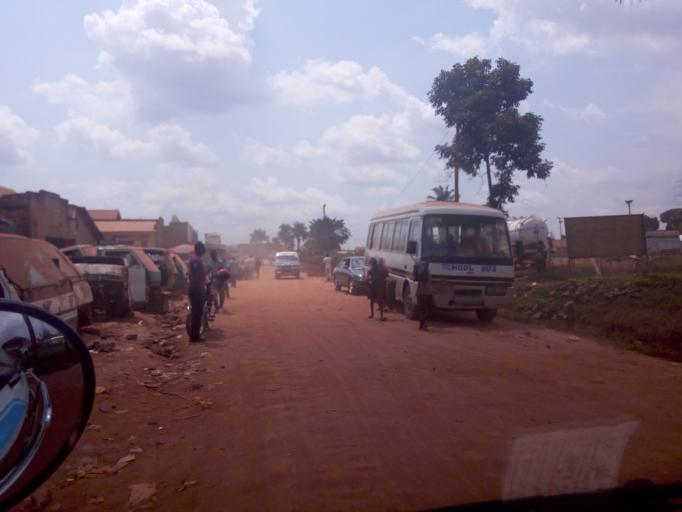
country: UG
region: Central Region
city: Kampala Central Division
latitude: 0.3471
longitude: 32.5587
